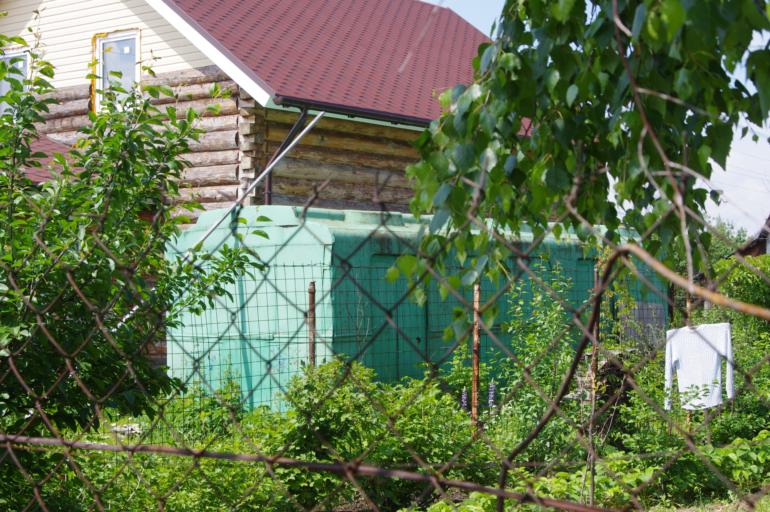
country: RU
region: Moskovskaya
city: Malyshevo
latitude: 55.5392
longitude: 38.2969
